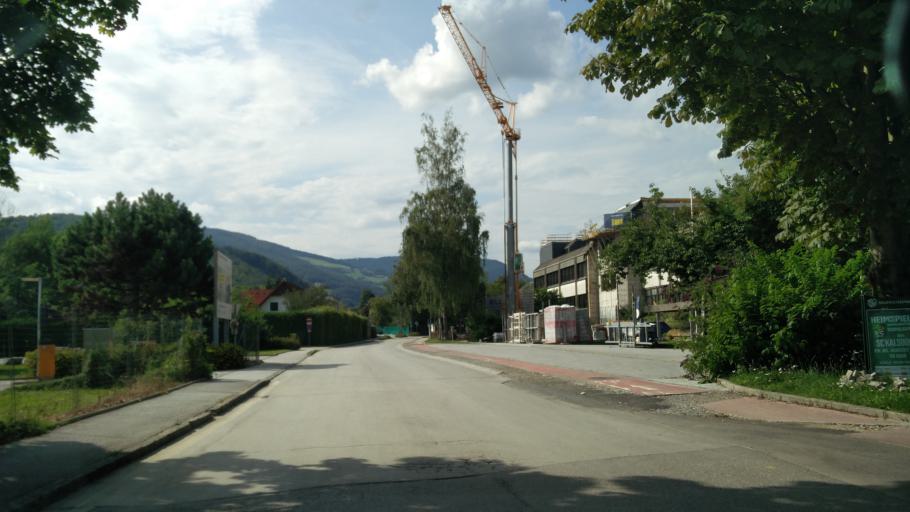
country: AT
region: Styria
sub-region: Politischer Bezirk Weiz
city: Weiz
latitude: 47.2234
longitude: 15.6235
